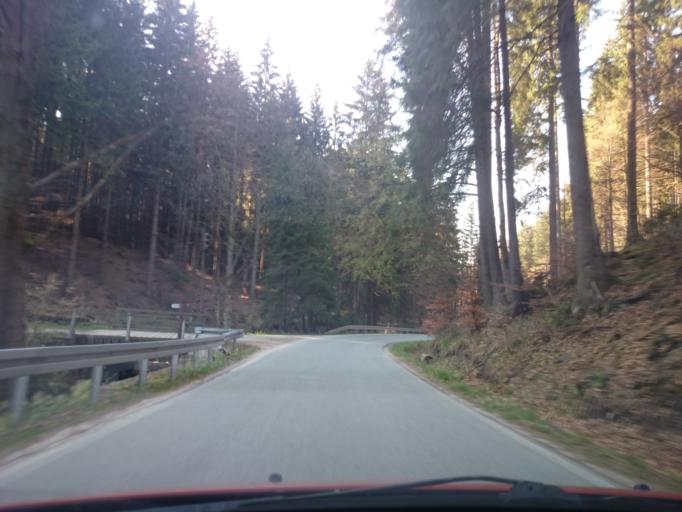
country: PL
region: Lower Silesian Voivodeship
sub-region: Powiat klodzki
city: Duszniki-Zdroj
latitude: 50.3590
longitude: 16.3945
